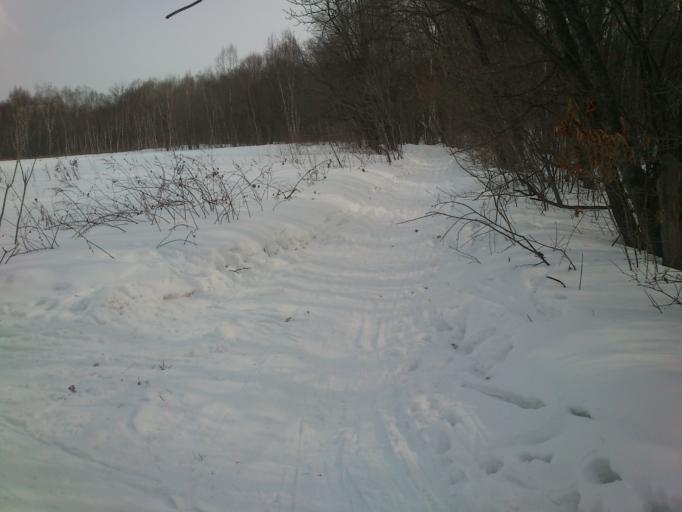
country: RU
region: Primorskiy
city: Volchanets
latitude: 43.1718
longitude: 132.7369
